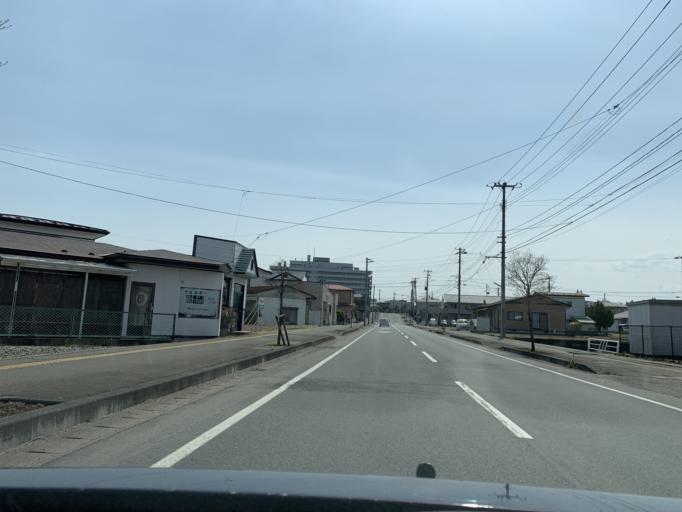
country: JP
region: Iwate
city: Mizusawa
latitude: 39.1264
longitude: 141.1353
